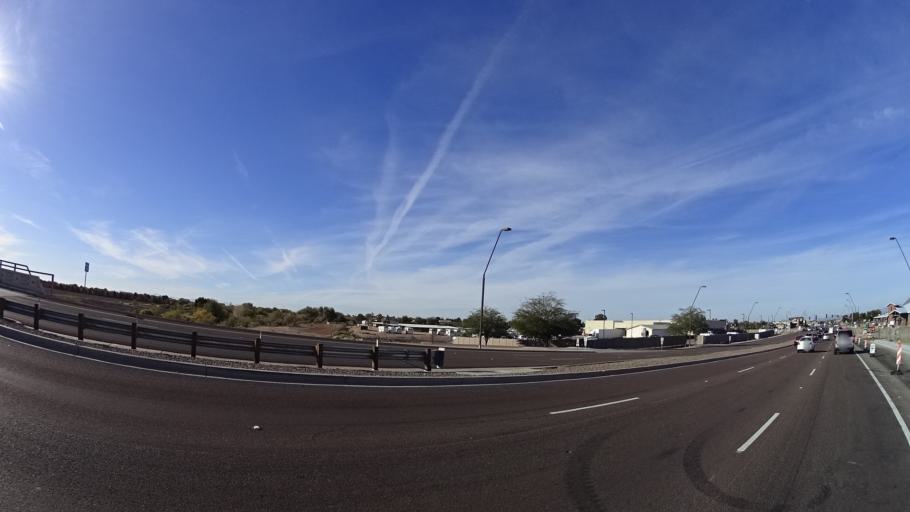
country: US
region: Arizona
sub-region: Maricopa County
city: Queen Creek
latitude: 33.2432
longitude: -111.6377
